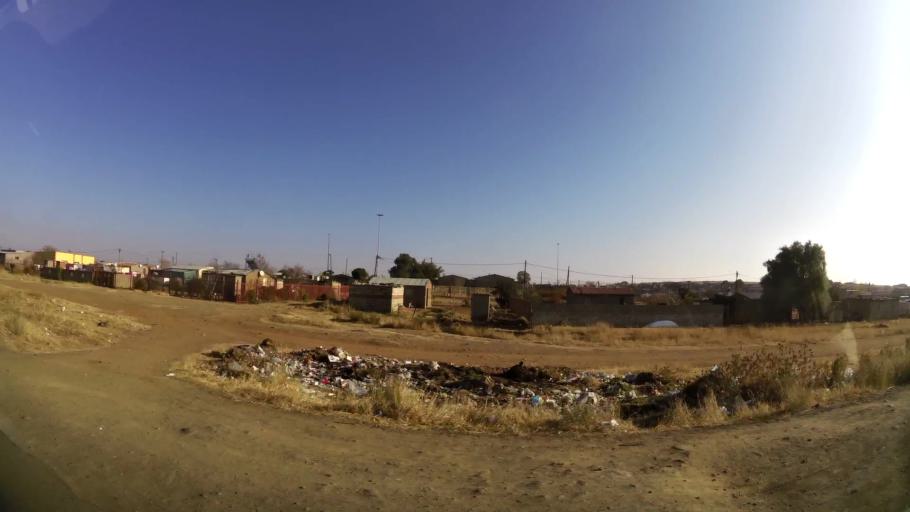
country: ZA
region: Orange Free State
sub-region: Mangaung Metropolitan Municipality
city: Bloemfontein
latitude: -29.1684
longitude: 26.2465
